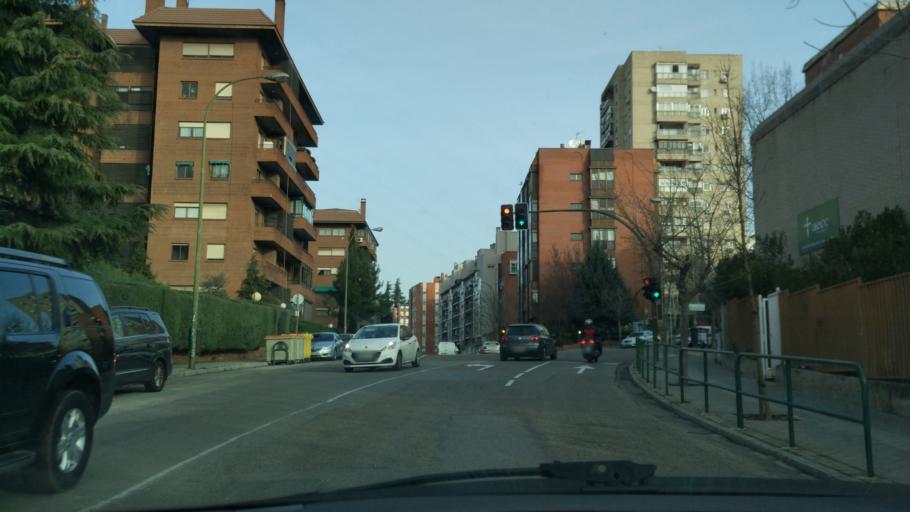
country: ES
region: Madrid
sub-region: Provincia de Madrid
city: Tetuan de las Victorias
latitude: 40.4545
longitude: -3.7145
